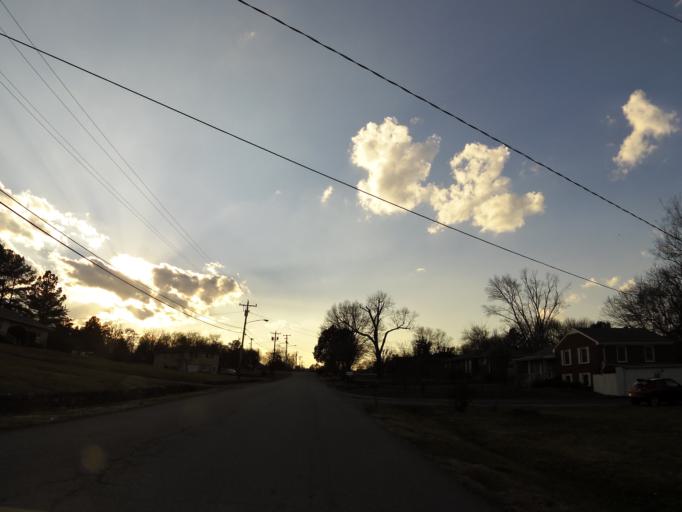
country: US
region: Tennessee
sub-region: Wilson County
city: Lebanon
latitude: 36.2137
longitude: -86.3397
